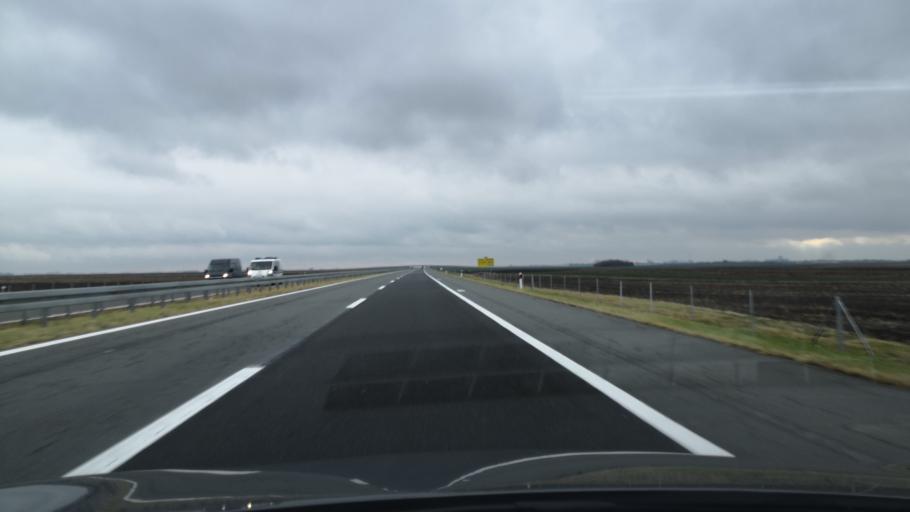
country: RS
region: Autonomna Pokrajina Vojvodina
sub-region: Severnobacki Okrug
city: Backa Topola
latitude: 45.8529
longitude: 19.6963
